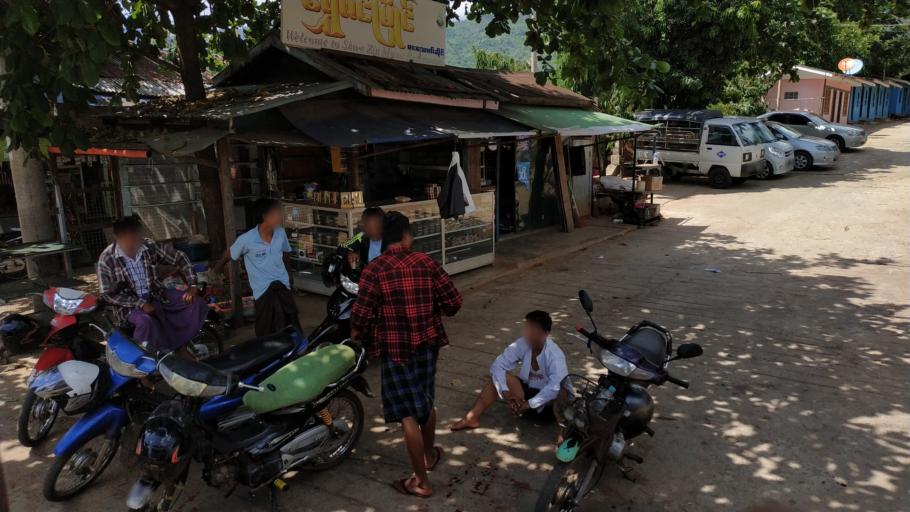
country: MM
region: Mon
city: Kyaikto
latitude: 17.4004
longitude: 97.0772
